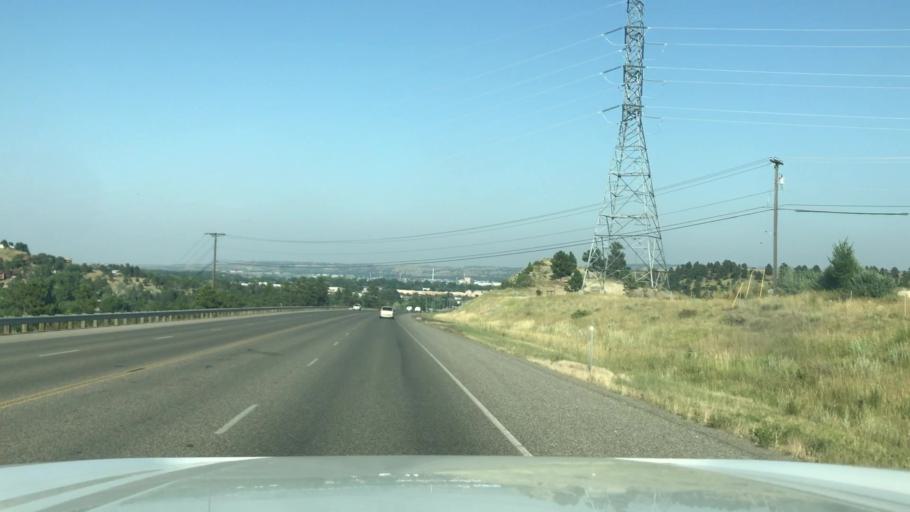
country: US
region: Montana
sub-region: Yellowstone County
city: Billings
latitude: 45.8001
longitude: -108.4955
